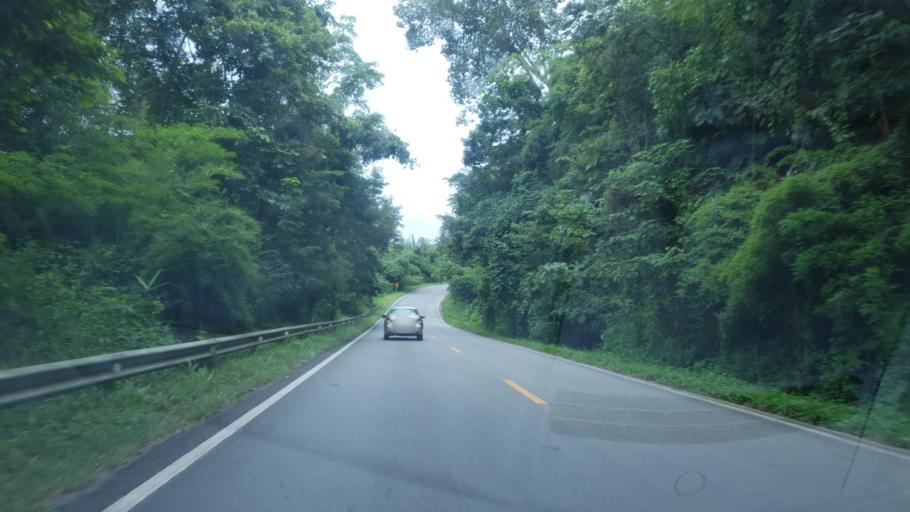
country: TH
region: Mae Hong Son
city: Khun Yuam
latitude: 18.7202
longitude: 97.9080
